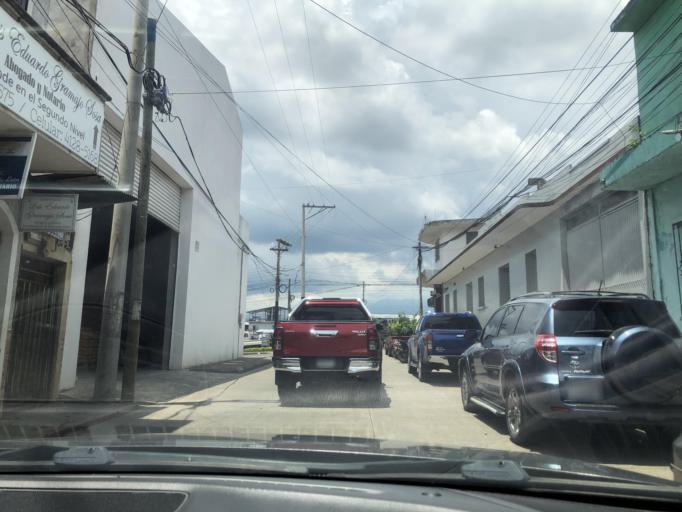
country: GT
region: Quetzaltenango
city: Coatepeque
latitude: 14.7041
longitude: -91.8658
